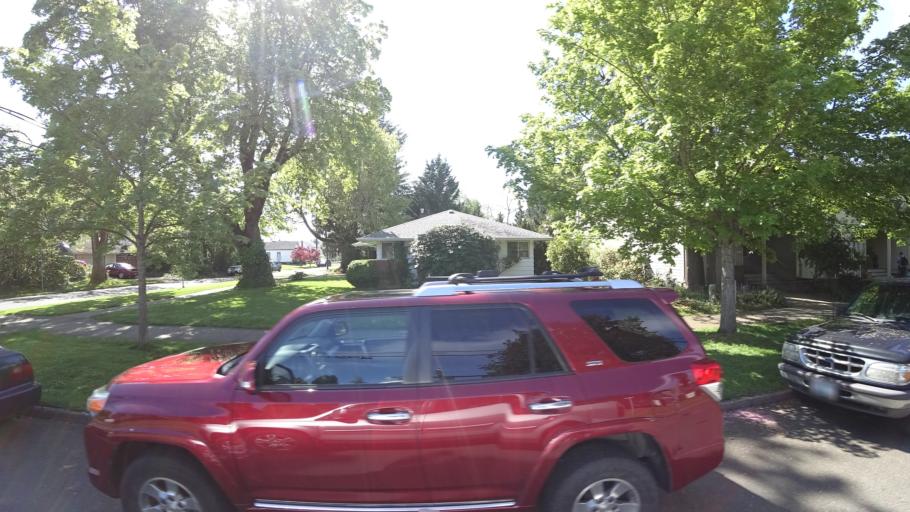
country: US
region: Oregon
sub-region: Washington County
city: Hillsboro
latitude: 45.5254
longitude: -122.9861
